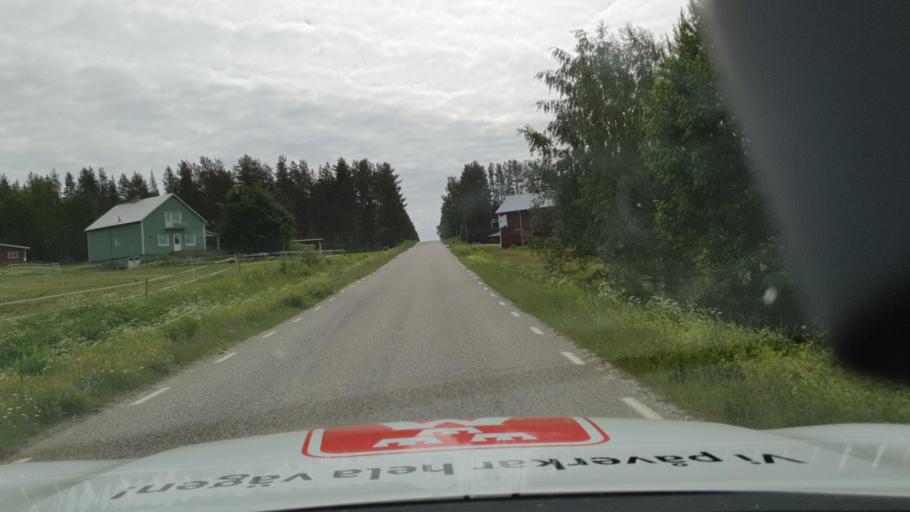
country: SE
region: Vaesterbotten
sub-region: Skelleftea Kommun
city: Forsbacka
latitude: 64.6306
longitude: 20.4784
